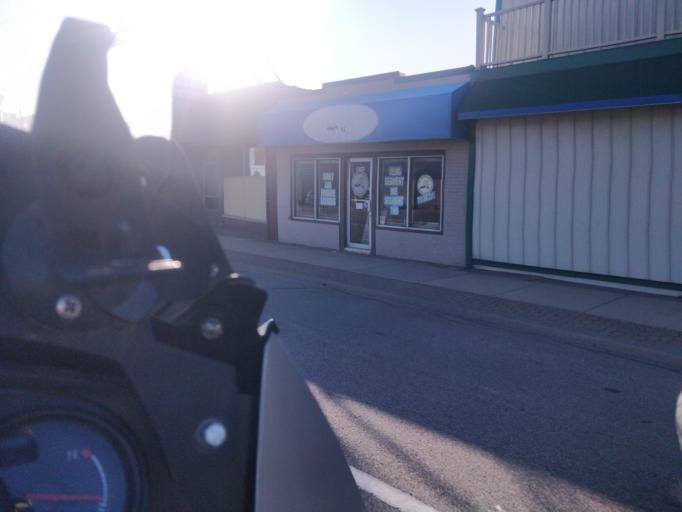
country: US
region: Michigan
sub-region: Wayne County
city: Melvindale
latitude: 42.2805
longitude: -83.1889
